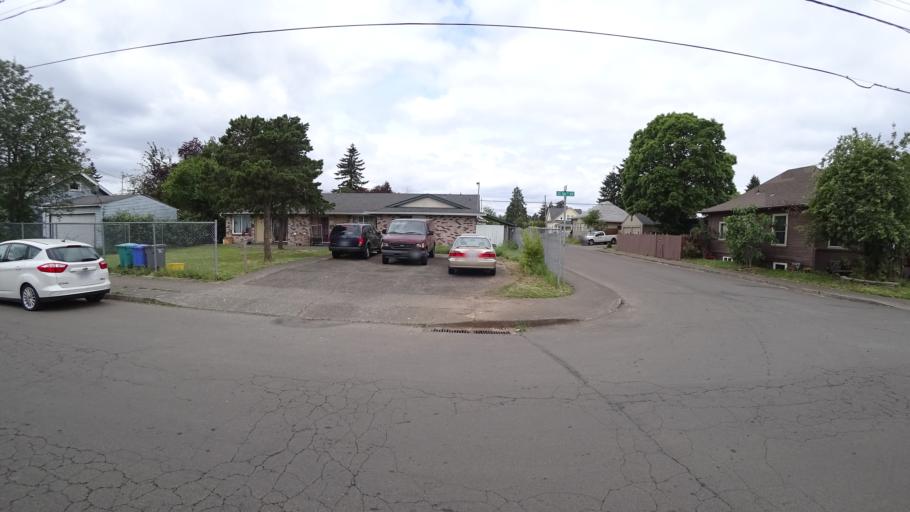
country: US
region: Oregon
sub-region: Multnomah County
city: Lents
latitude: 45.4805
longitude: -122.5749
